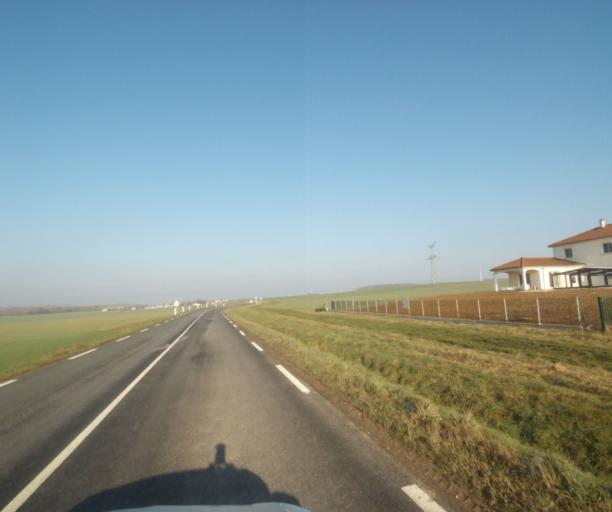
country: FR
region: Champagne-Ardenne
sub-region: Departement de la Haute-Marne
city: Wassy
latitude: 48.5143
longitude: 4.9364
